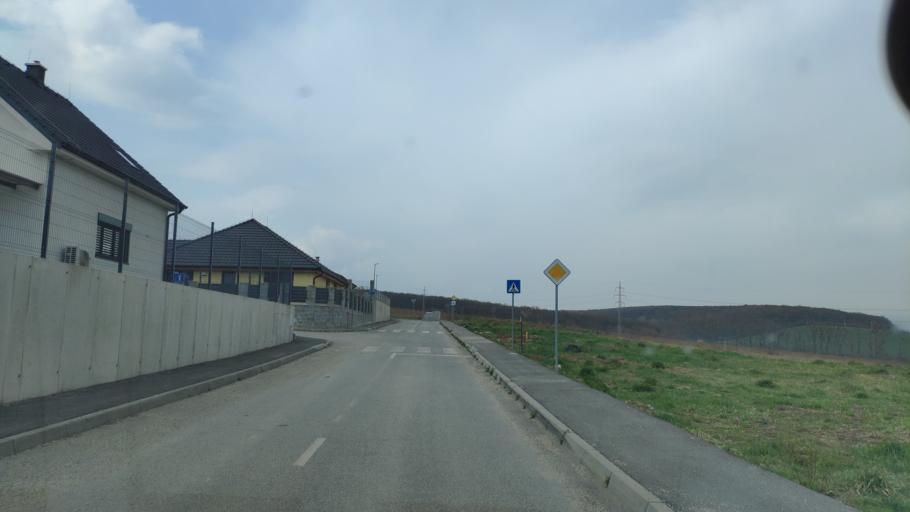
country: SK
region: Kosicky
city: Kosice
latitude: 48.6822
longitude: 21.3097
